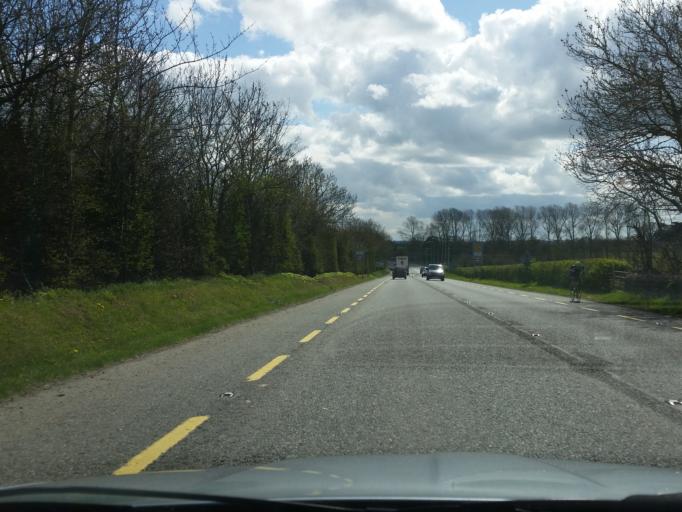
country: IE
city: Kentstown
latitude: 53.6259
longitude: -6.4894
